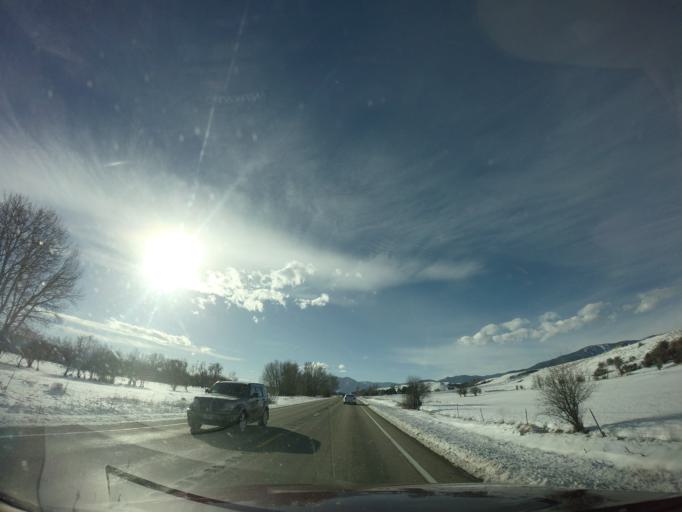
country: US
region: Montana
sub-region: Carbon County
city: Red Lodge
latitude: 45.2416
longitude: -109.2358
